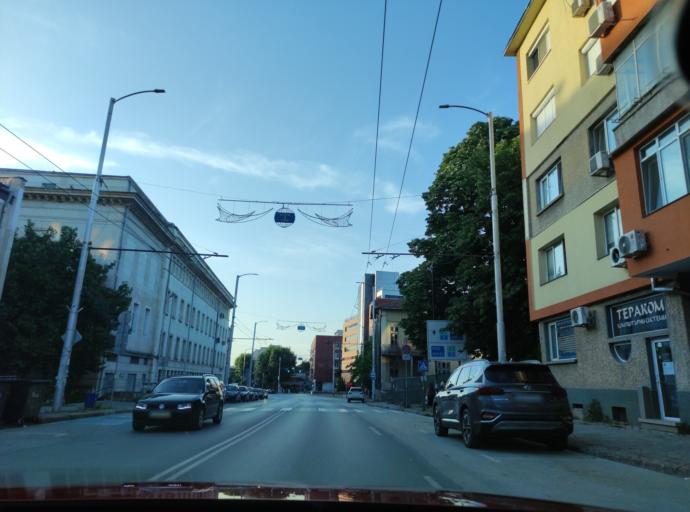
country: BG
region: Pleven
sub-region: Obshtina Pleven
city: Pleven
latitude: 43.4069
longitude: 24.6213
